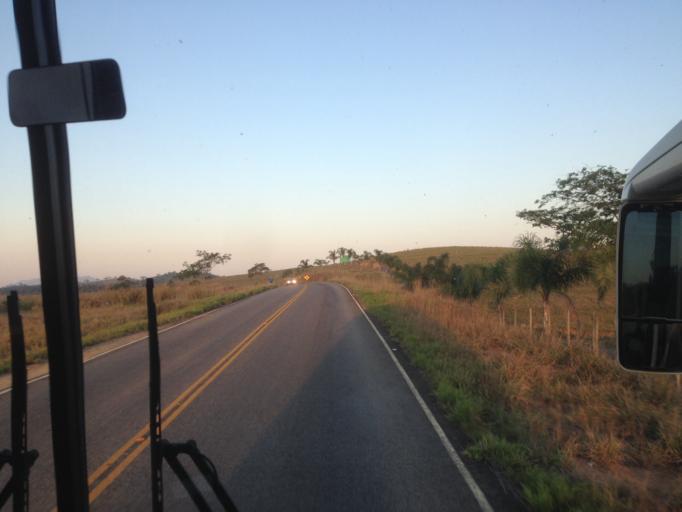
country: BR
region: Minas Gerais
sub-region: Rio Novo
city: Rio Novo
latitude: -21.5205
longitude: -43.1681
